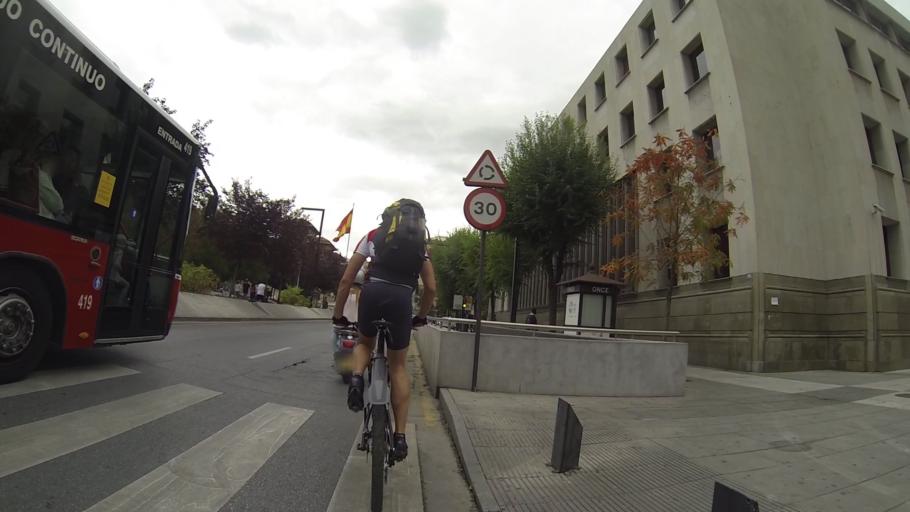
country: ES
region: Andalusia
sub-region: Provincia de Granada
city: Granada
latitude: 37.1833
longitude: -3.6030
